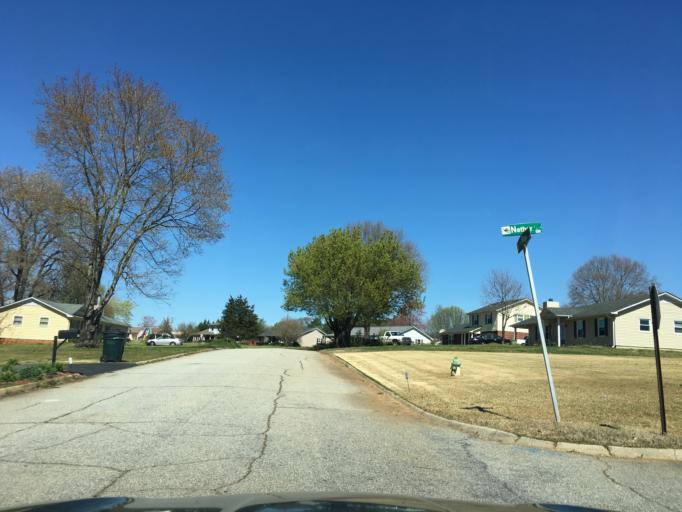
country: US
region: South Carolina
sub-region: Spartanburg County
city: Wellford
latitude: 34.8830
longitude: -82.0673
